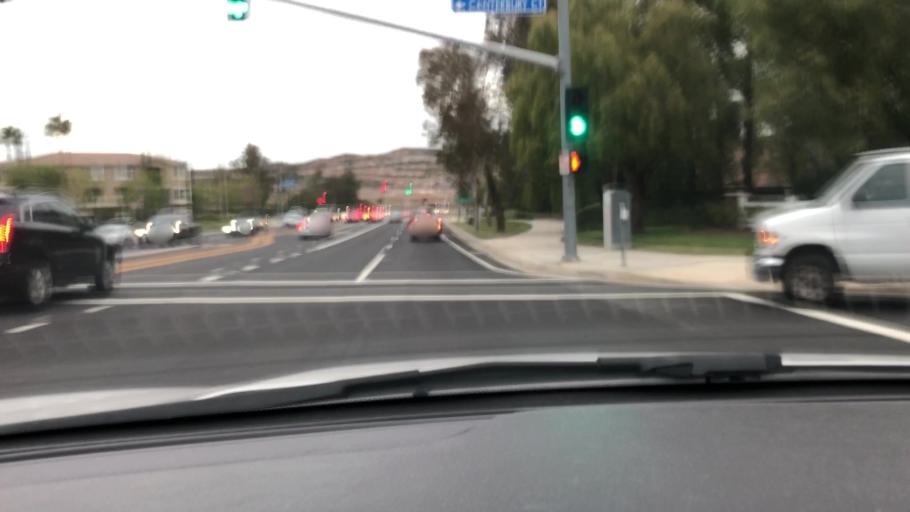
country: US
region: California
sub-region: Los Angeles County
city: Valencia
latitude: 34.4623
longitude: -118.5480
